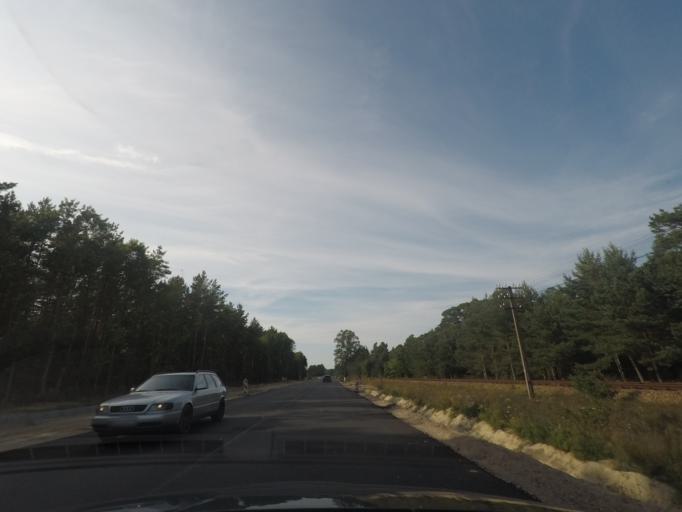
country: PL
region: Pomeranian Voivodeship
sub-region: Powiat leborski
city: Leba
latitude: 54.7214
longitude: 17.5725
